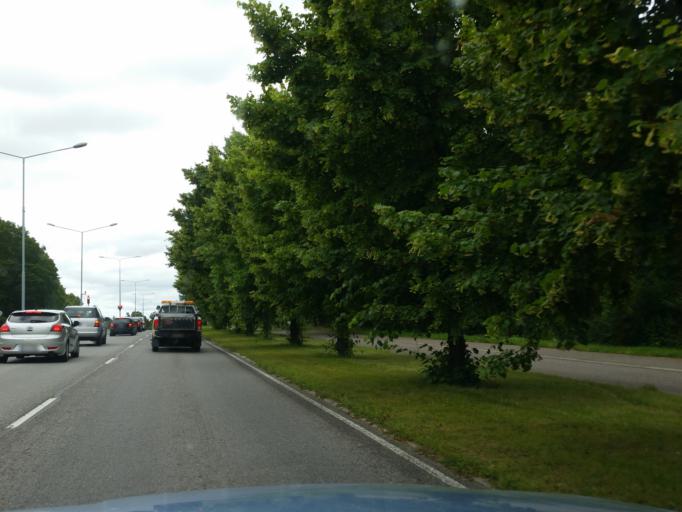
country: FI
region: Varsinais-Suomi
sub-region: Turku
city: Turku
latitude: 60.4325
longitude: 22.2998
